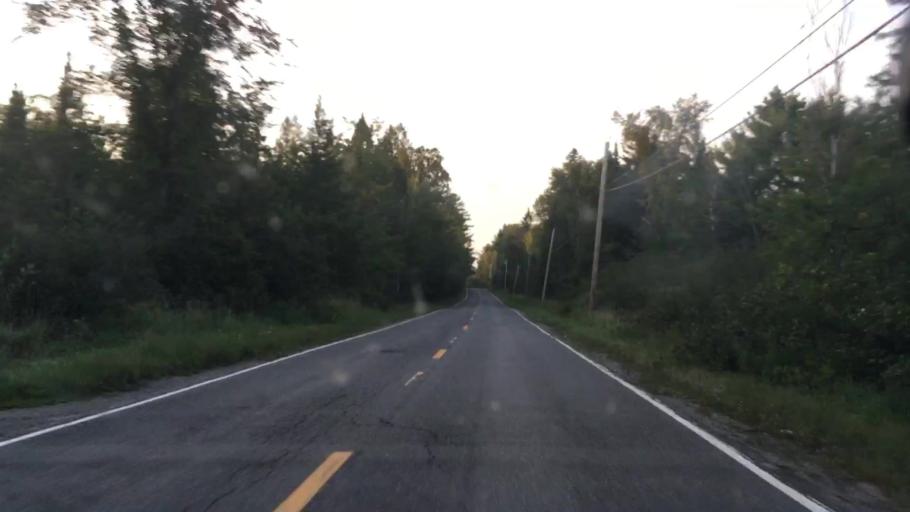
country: US
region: Maine
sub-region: Penobscot County
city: Hermon
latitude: 44.7044
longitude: -68.9477
